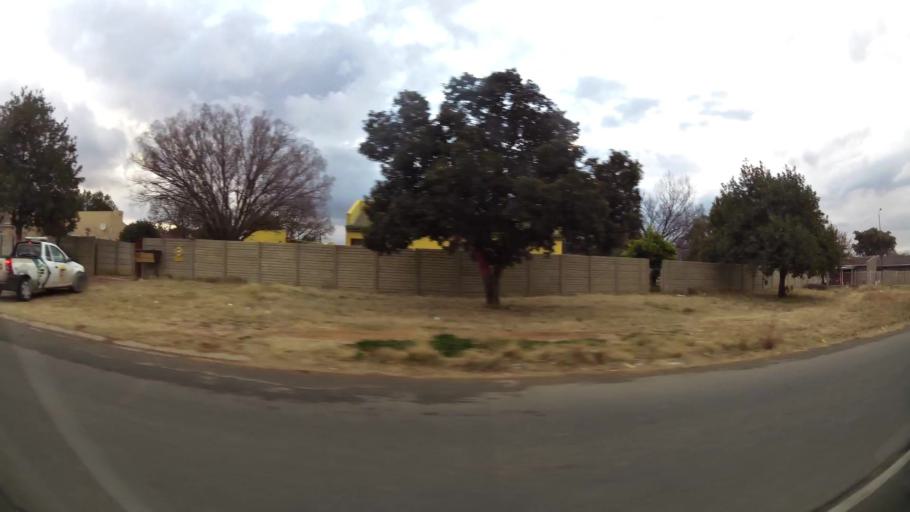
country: ZA
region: Orange Free State
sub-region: Lejweleputswa District Municipality
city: Welkom
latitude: -27.9508
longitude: 26.7349
